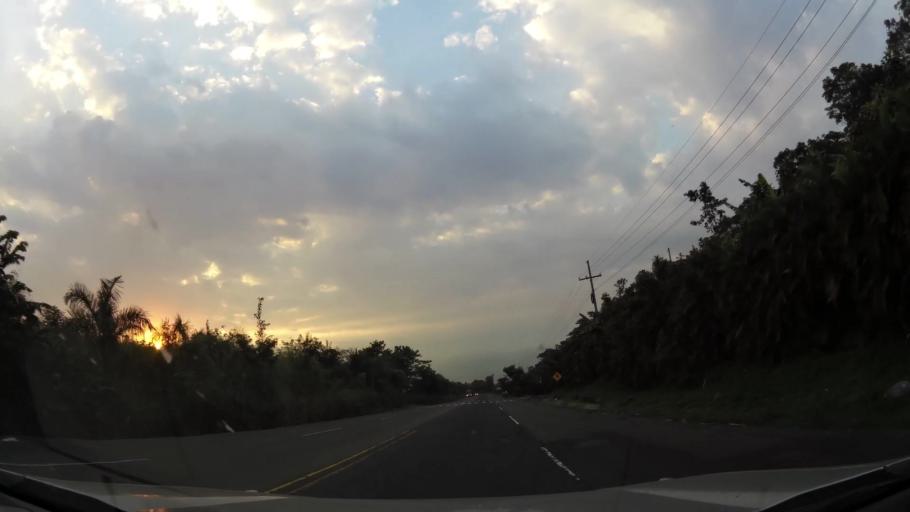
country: GT
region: Escuintla
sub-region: Municipio de La Democracia
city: La Democracia
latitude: 14.2744
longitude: -90.9112
